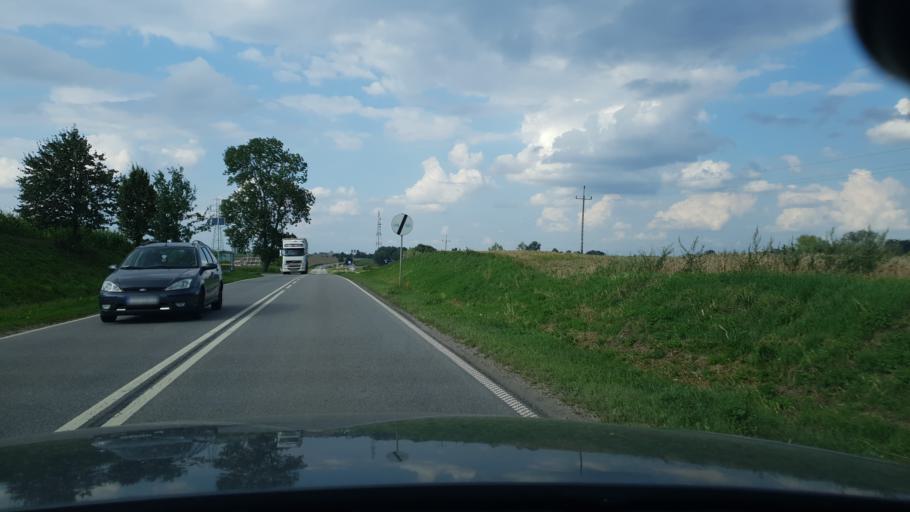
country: PL
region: Kujawsko-Pomorskie
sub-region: Powiat grudziadzki
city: Radzyn Chelminski
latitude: 53.3665
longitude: 18.9363
